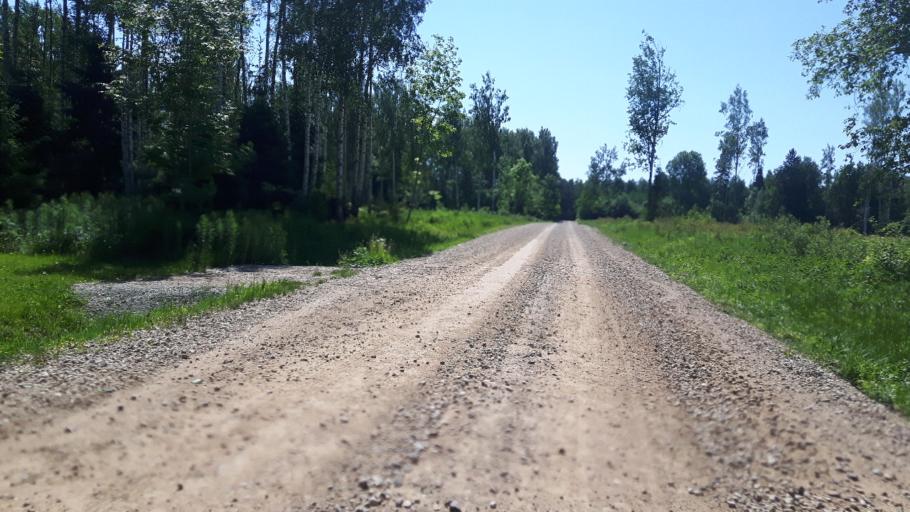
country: EE
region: Paernumaa
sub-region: Tootsi vald
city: Tootsi
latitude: 58.5121
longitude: 24.9089
